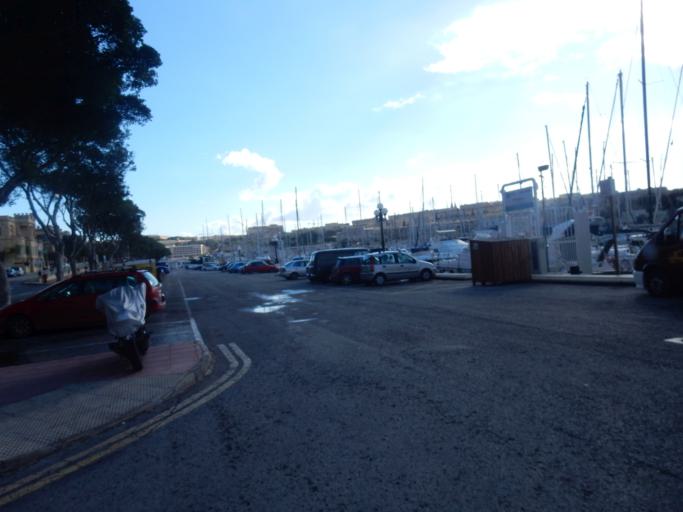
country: MT
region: Ta' Xbiex
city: Ta' Xbiex
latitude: 35.8979
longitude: 14.4961
